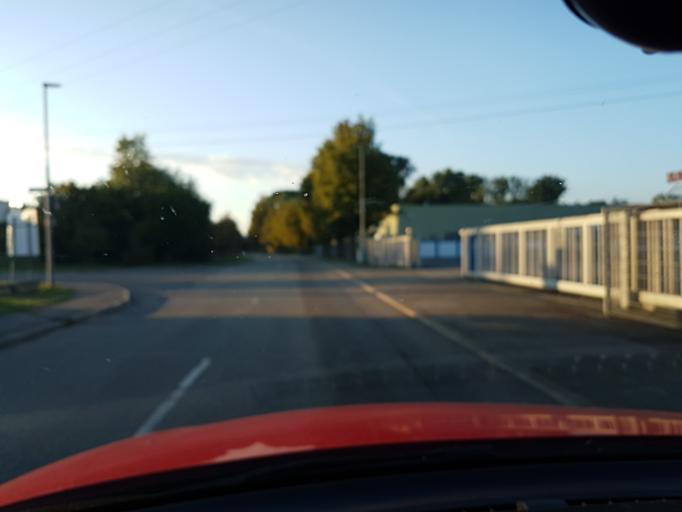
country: DE
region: Baden-Wuerttemberg
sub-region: Regierungsbezirk Stuttgart
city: Eppingen
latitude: 49.1021
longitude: 8.8969
